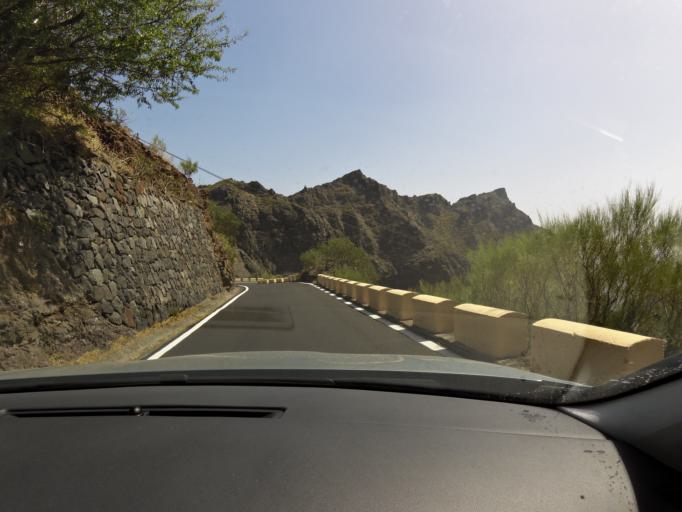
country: ES
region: Canary Islands
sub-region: Provincia de Santa Cruz de Tenerife
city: Santiago del Teide
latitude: 28.3038
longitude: -16.8307
